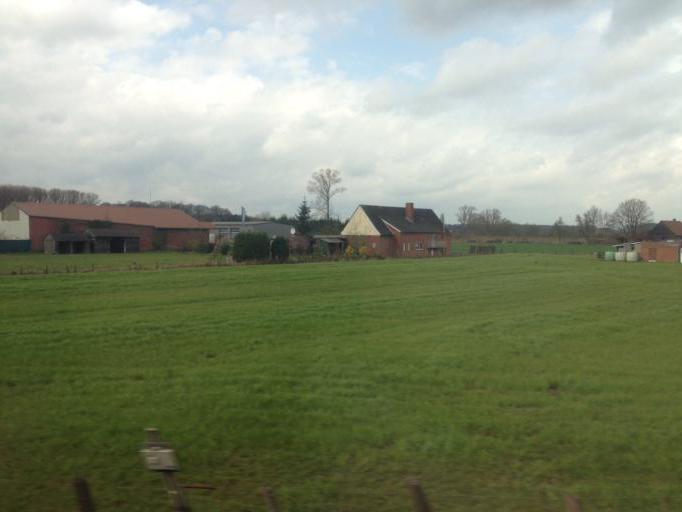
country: DE
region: North Rhine-Westphalia
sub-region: Regierungsbezirk Munster
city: Dulmen
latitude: 51.8553
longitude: 7.3492
